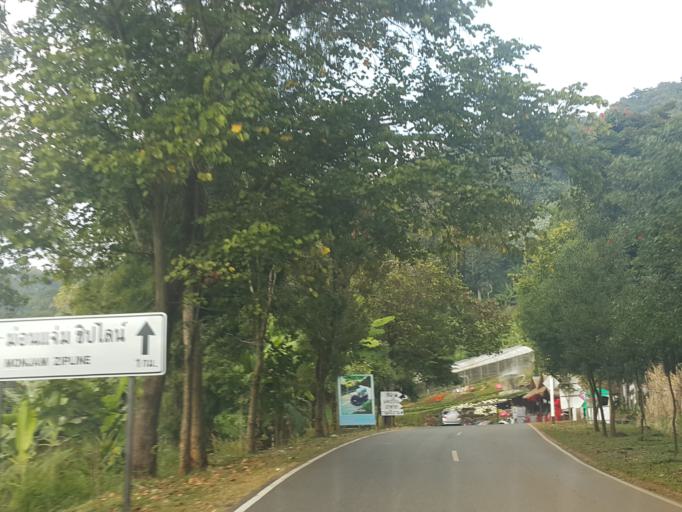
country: TH
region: Chiang Mai
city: Samoeng
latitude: 18.9098
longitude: 98.8280
